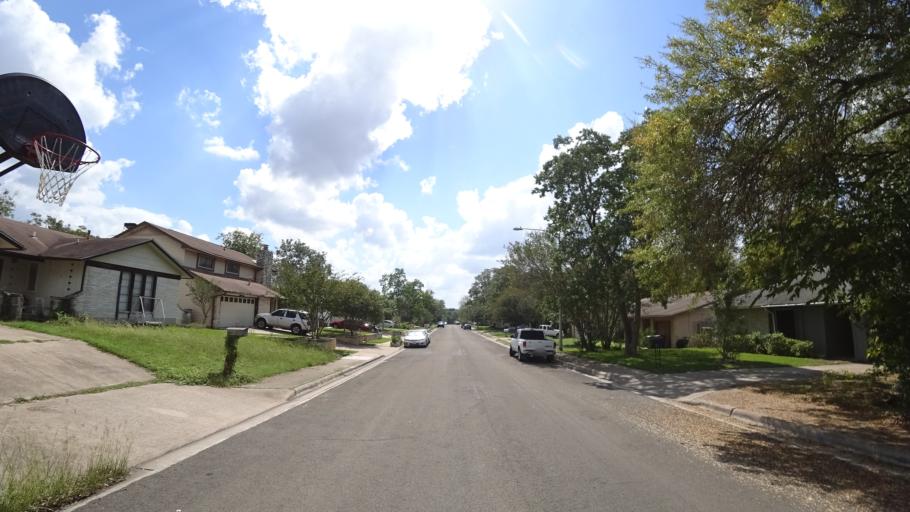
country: US
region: Texas
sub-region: Travis County
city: Onion Creek
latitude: 30.1890
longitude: -97.7877
